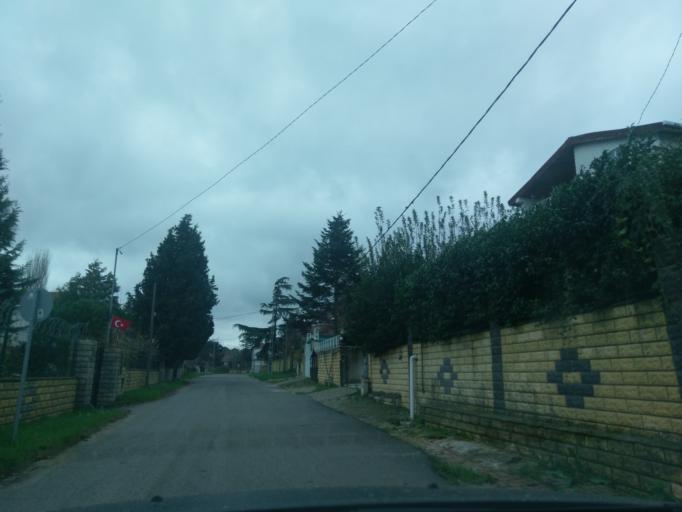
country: TR
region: Istanbul
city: Catalca
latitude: 41.1598
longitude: 28.4444
